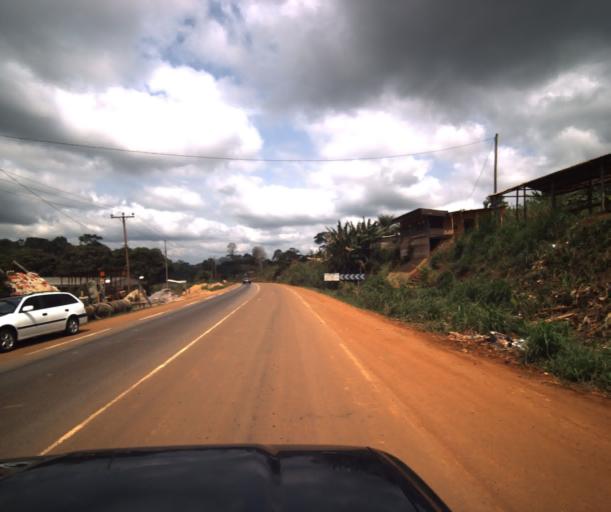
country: CM
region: Centre
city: Mbankomo
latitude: 3.7909
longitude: 11.3979
